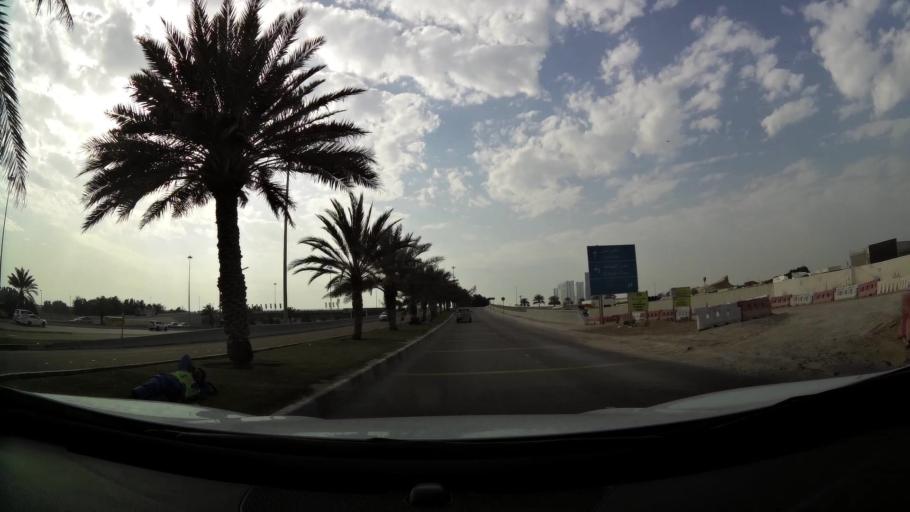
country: AE
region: Abu Dhabi
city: Abu Dhabi
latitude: 24.4074
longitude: 54.4740
